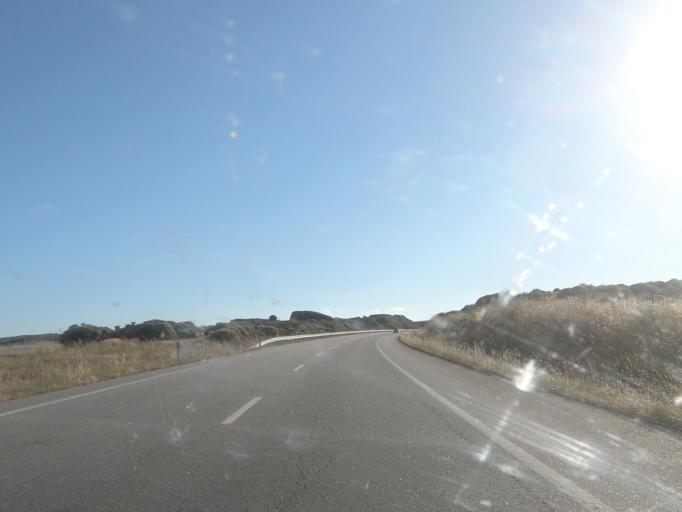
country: PT
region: Guarda
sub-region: Guarda
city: Sequeira
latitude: 40.6018
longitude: -7.0890
